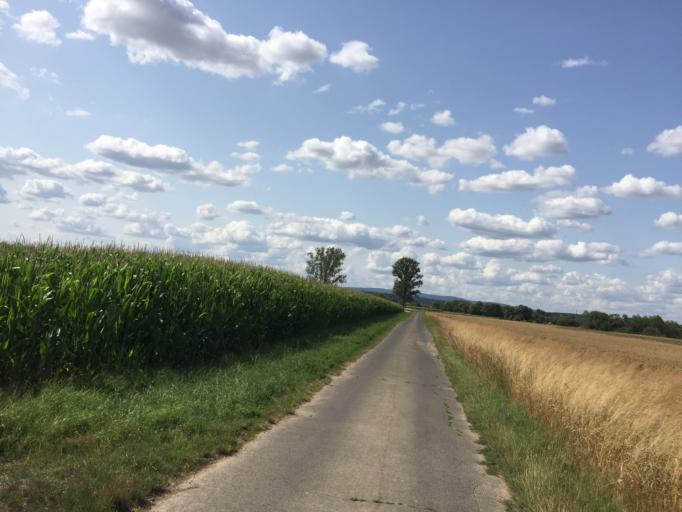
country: DE
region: Hesse
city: Schwalmstadt
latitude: 50.8993
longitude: 9.2587
